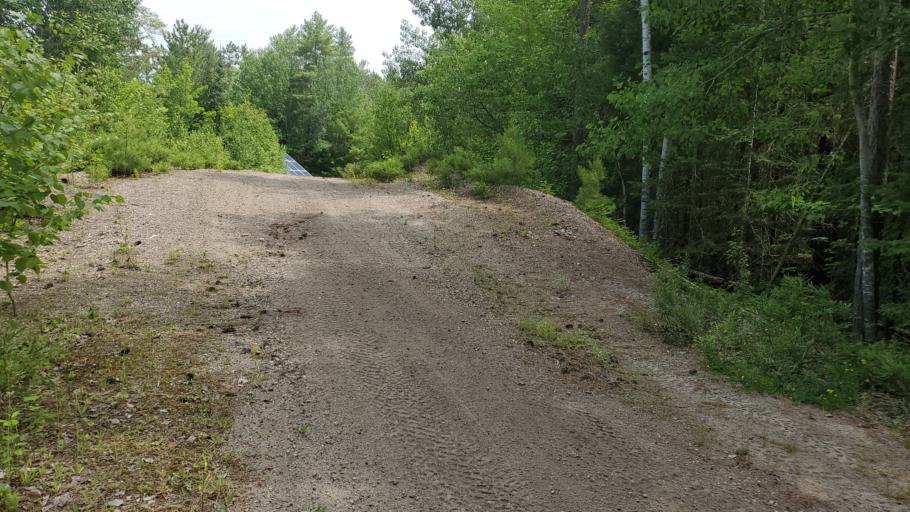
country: CA
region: Ontario
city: Mattawa
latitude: 46.2621
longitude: -78.2745
